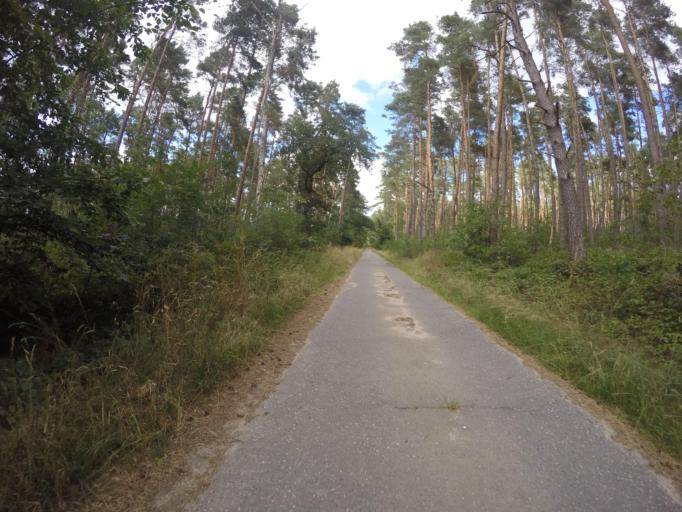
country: DE
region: Lower Saxony
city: Thomasburg
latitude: 53.2429
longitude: 10.6712
